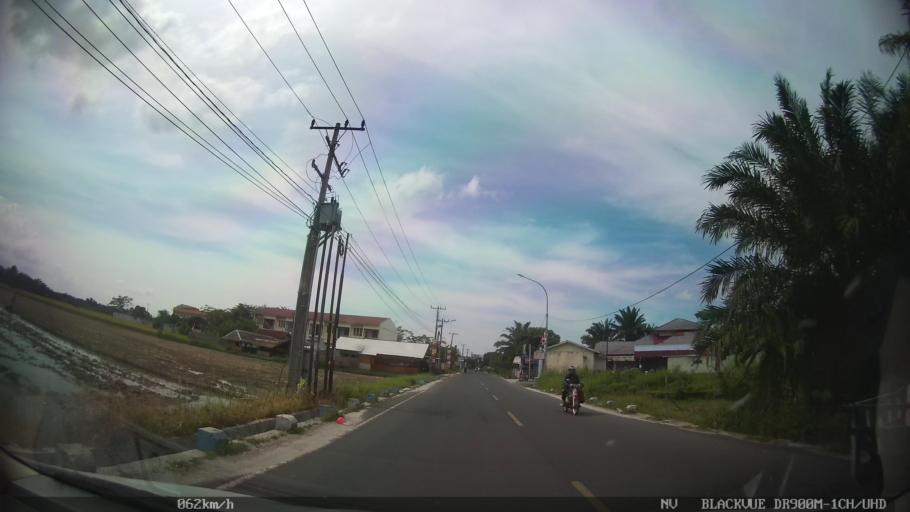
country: ID
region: North Sumatra
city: Percut
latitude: 3.5884
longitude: 98.8598
